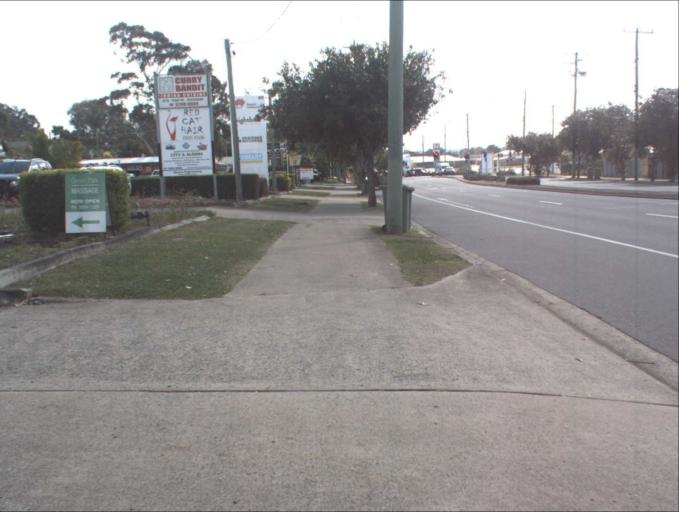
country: AU
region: Queensland
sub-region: Logan
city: Waterford West
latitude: -27.6888
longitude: 153.1367
